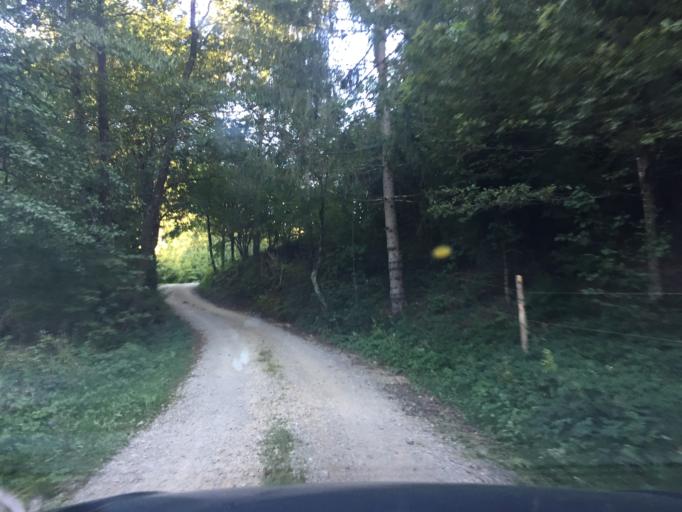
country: SI
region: Postojna
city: Postojna
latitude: 45.8117
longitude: 14.1309
